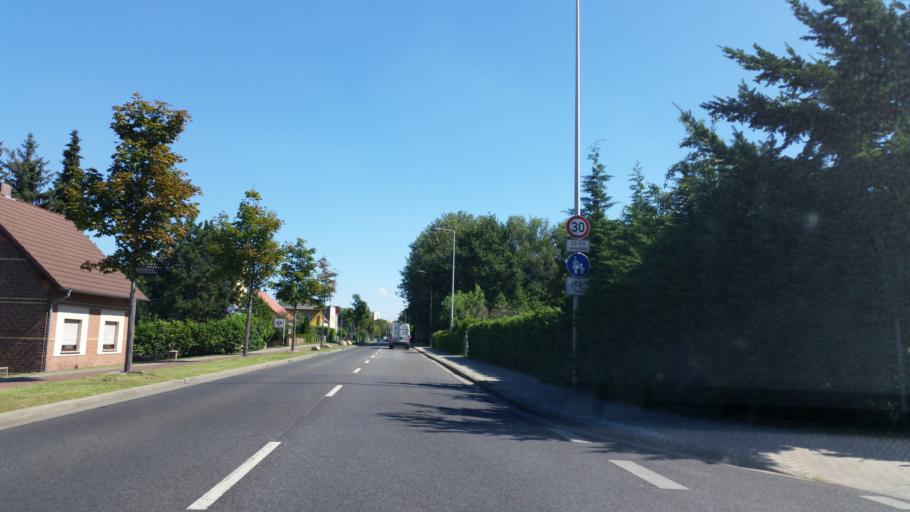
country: DE
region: Brandenburg
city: Cottbus
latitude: 51.7307
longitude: 14.3116
